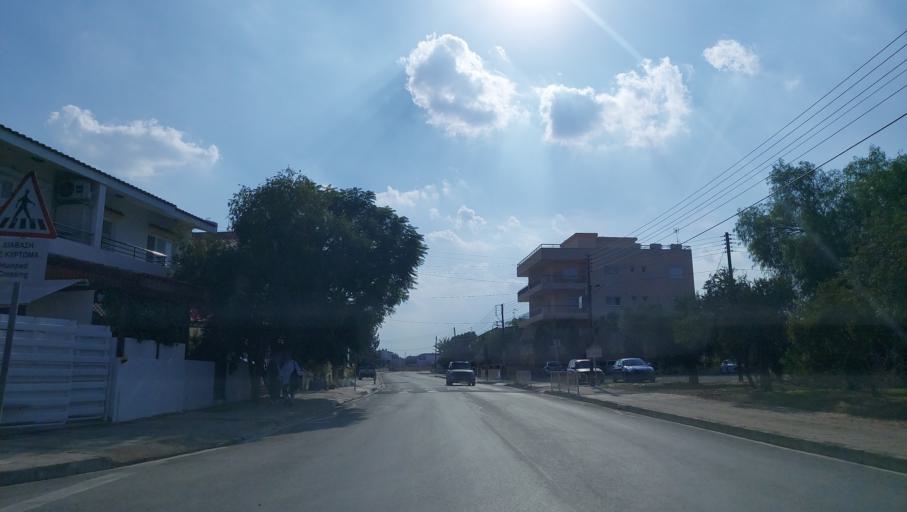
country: CY
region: Lefkosia
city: Tseri
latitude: 35.1091
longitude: 33.3100
